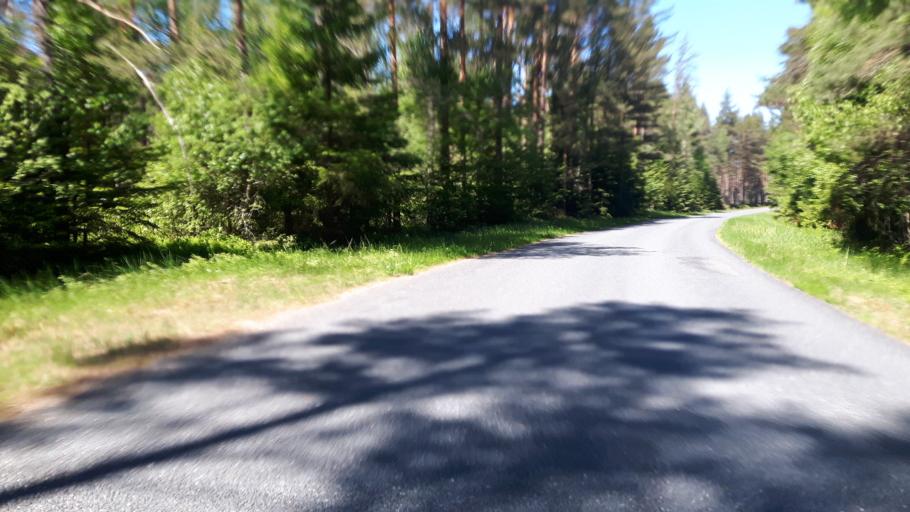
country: EE
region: Harju
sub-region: Loksa linn
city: Loksa
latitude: 59.5737
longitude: 25.6136
